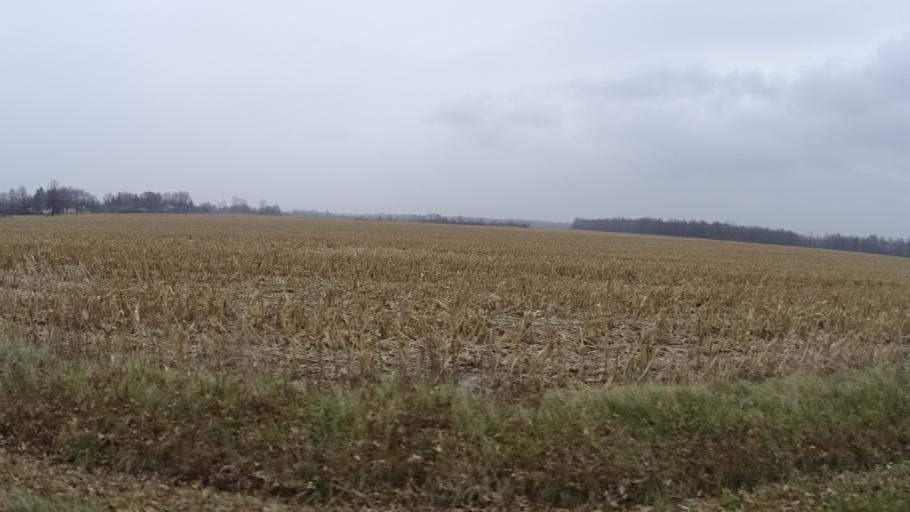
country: US
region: Ohio
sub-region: Lorain County
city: Amherst
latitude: 41.3501
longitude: -82.1955
